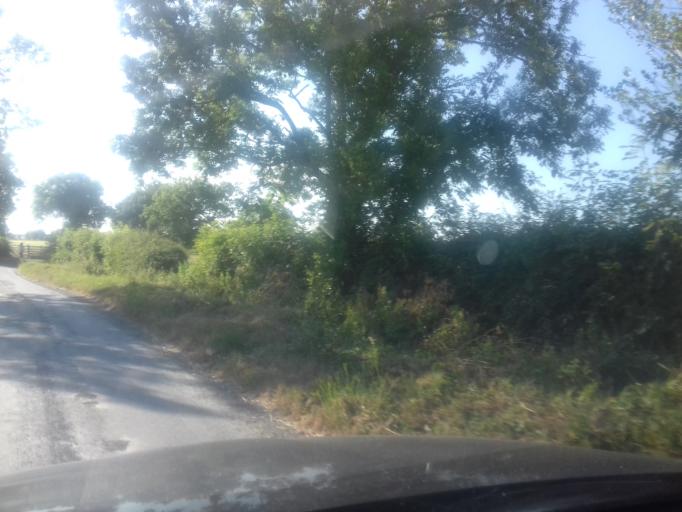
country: IE
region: Leinster
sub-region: Fingal County
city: Blanchardstown
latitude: 53.4417
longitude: -6.3698
